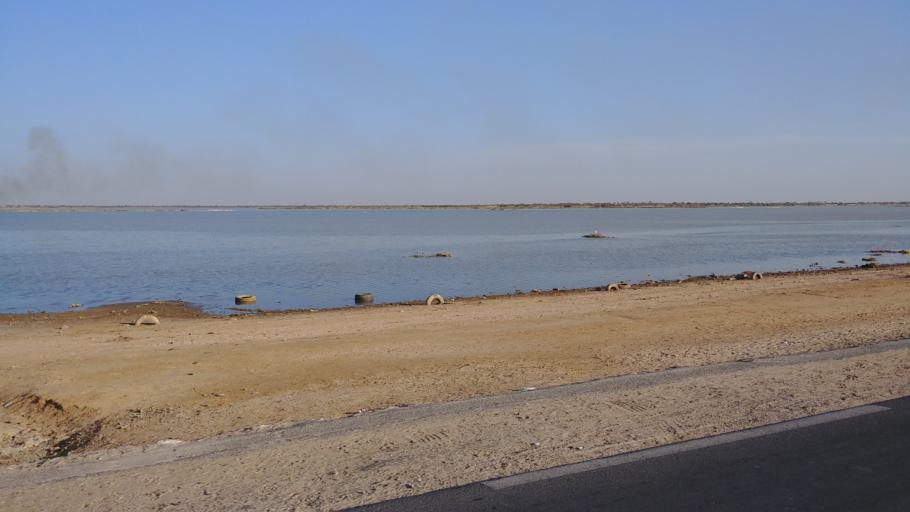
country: SN
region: Saint-Louis
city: Saint-Louis
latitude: 16.0224
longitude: -16.4828
